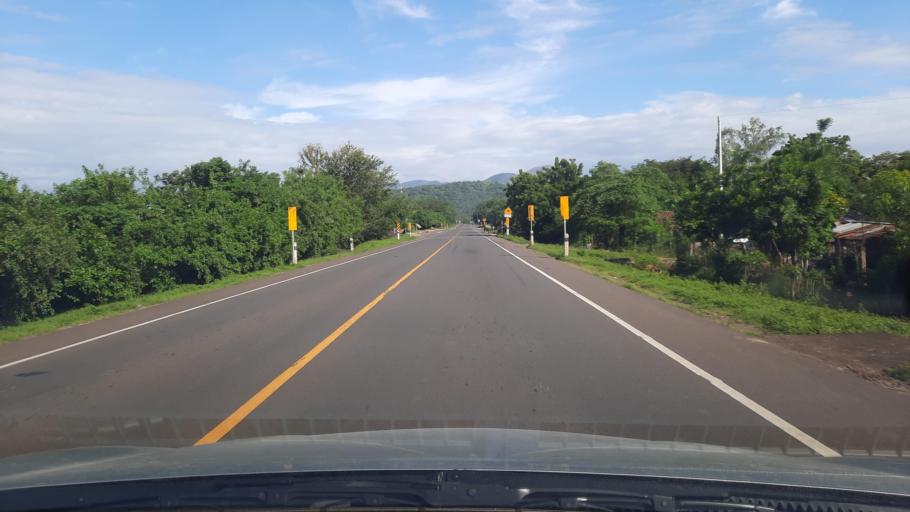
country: NI
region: Leon
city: Telica
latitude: 12.7134
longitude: -86.8743
